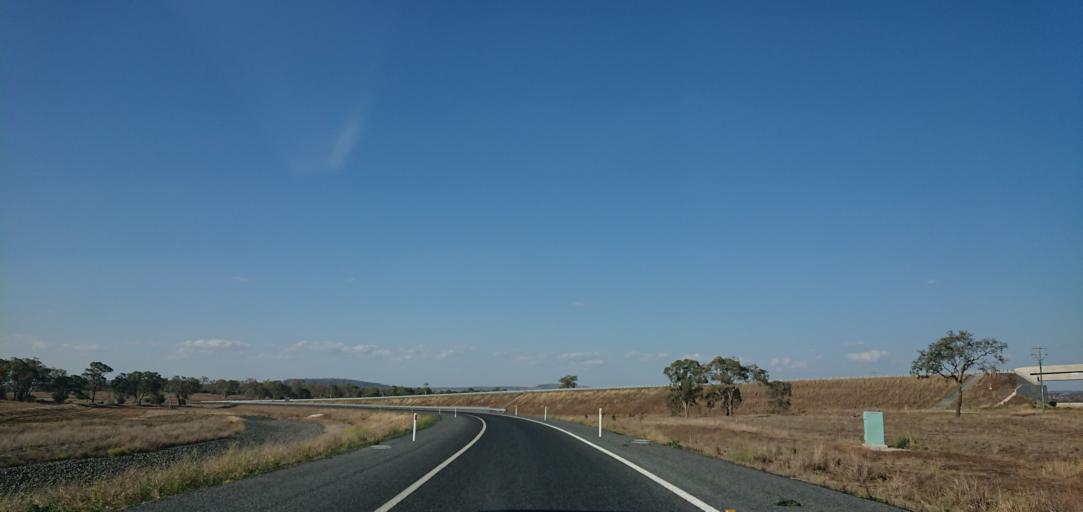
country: AU
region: Queensland
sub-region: Toowoomba
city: Westbrook
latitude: -27.6152
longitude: 151.7839
